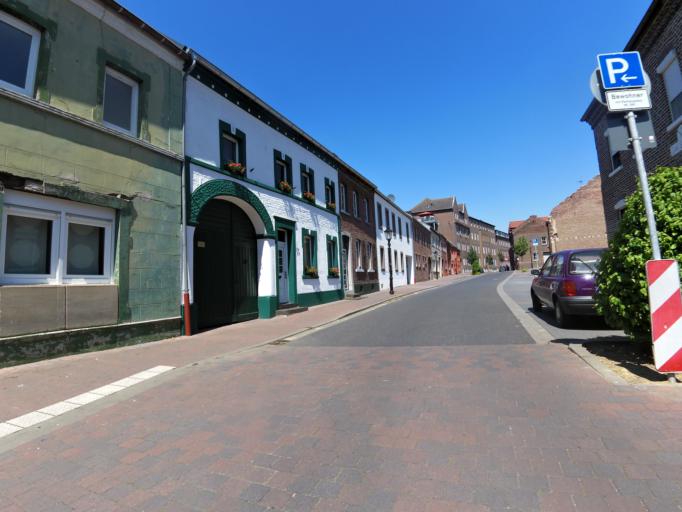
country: DE
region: North Rhine-Westphalia
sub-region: Regierungsbezirk Koln
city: Gangelt
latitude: 50.9914
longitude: 5.9952
